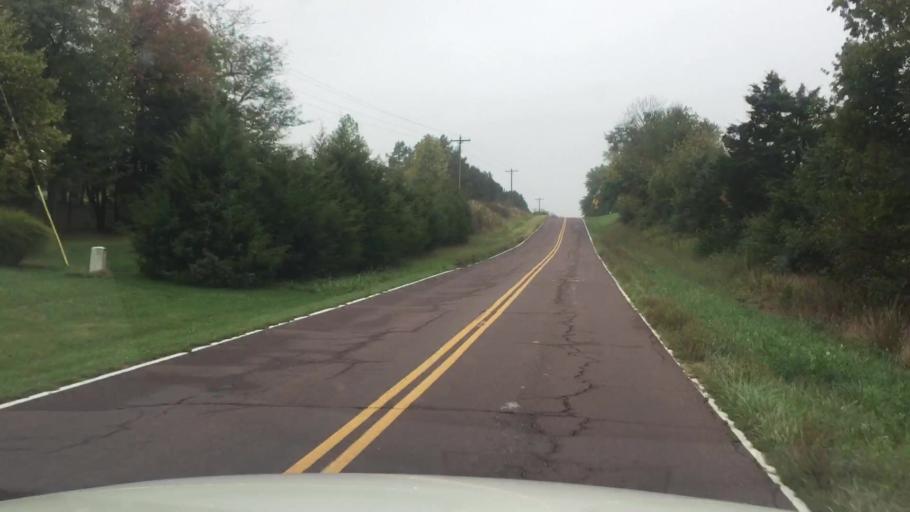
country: US
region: Missouri
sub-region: Boone County
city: Ashland
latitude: 38.8449
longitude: -92.3371
